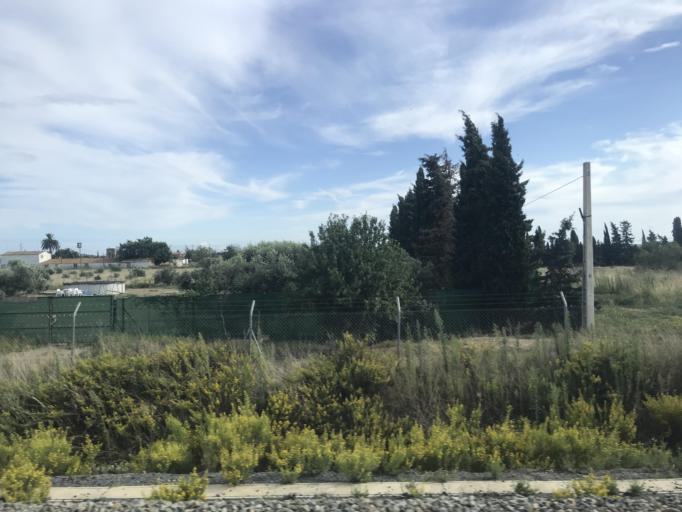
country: ES
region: Catalonia
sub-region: Provincia de Tarragona
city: Cambrils
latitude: 41.0950
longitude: 1.0859
